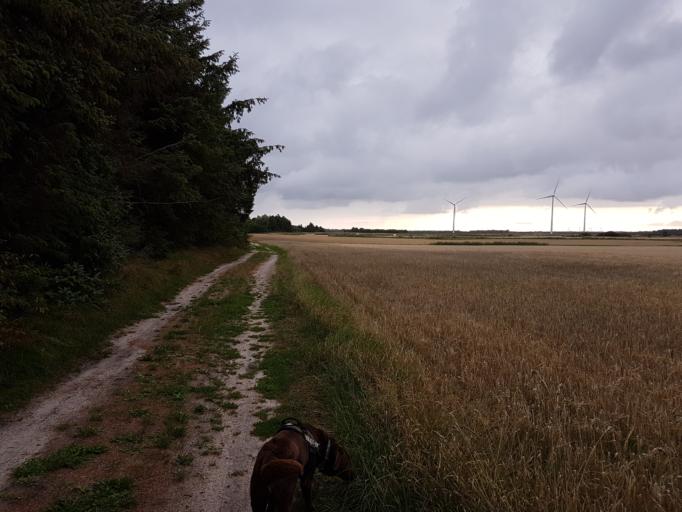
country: DK
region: Central Jutland
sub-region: Ringkobing-Skjern Kommune
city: Skjern
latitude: 55.8567
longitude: 8.2991
